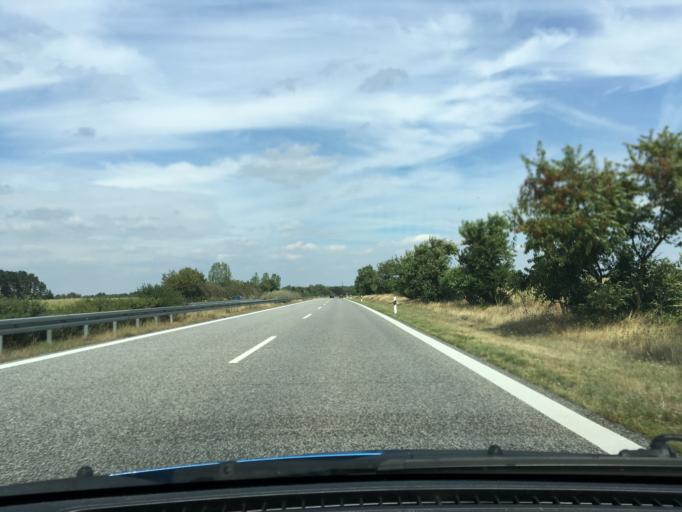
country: DE
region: Mecklenburg-Vorpommern
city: Plate
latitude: 53.5423
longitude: 11.4712
